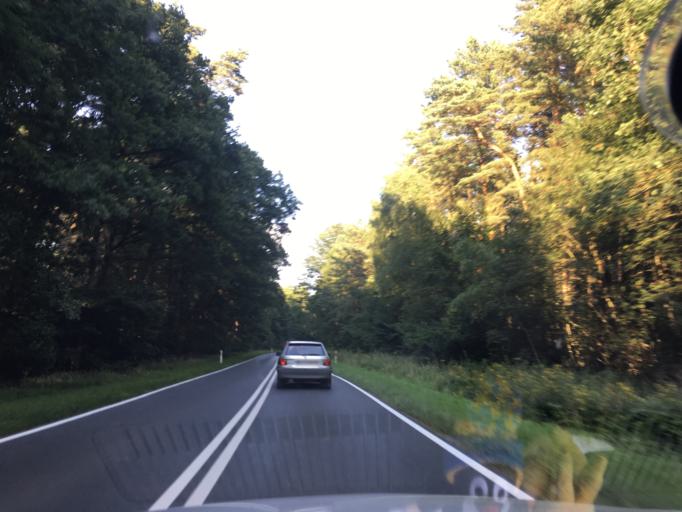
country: PL
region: West Pomeranian Voivodeship
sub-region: Powiat kamienski
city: Dziwnow
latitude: 54.0369
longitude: 14.8324
